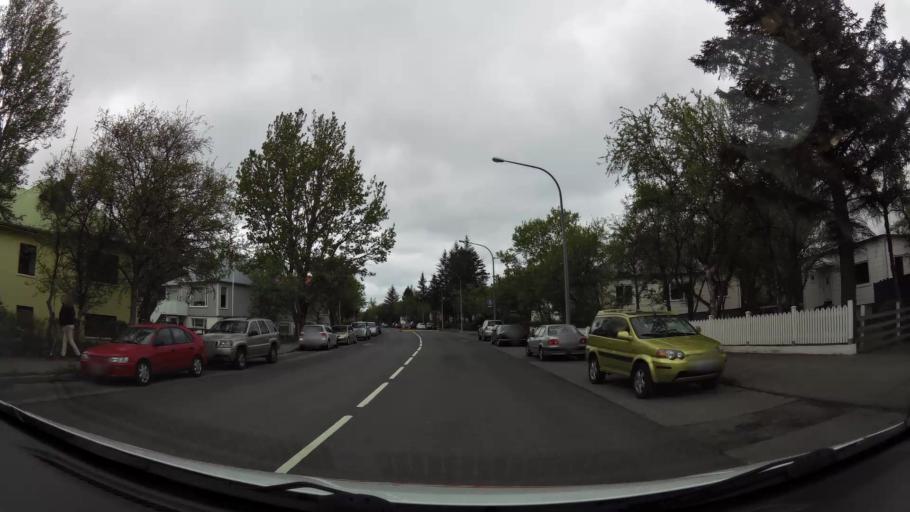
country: IS
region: Capital Region
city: Reykjavik
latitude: 64.1313
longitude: -21.8523
